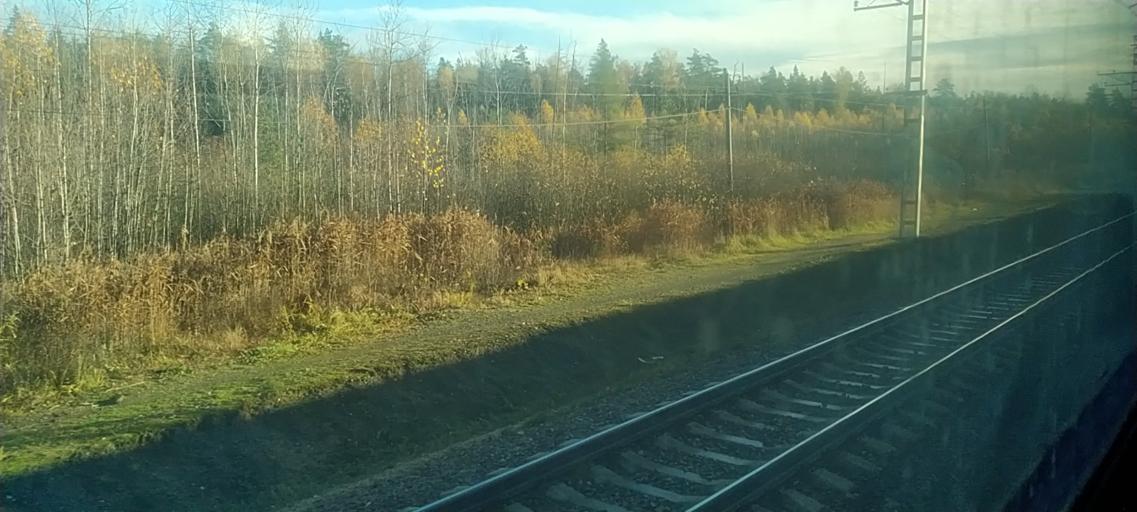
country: RU
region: Moskovskaya
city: Ramenskoye
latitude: 55.6381
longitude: 38.2634
